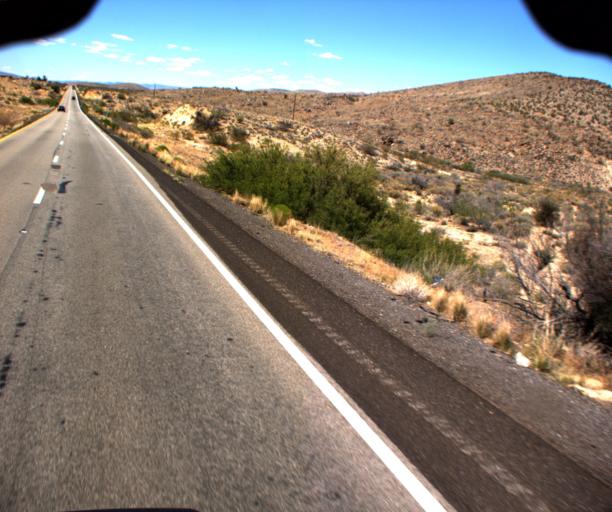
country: US
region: Arizona
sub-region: Mohave County
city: Kingman
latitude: 34.9679
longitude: -113.6700
